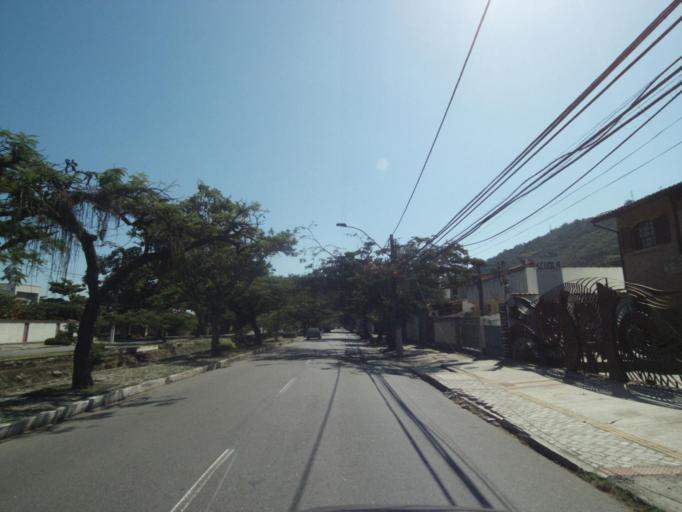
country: BR
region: Rio de Janeiro
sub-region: Niteroi
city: Niteroi
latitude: -22.9139
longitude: -43.0851
